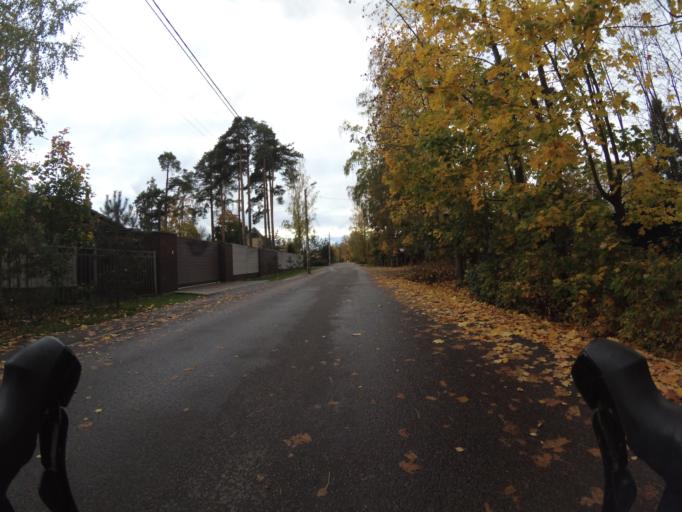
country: RU
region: St.-Petersburg
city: Lakhtinskiy
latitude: 59.9980
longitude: 30.1469
